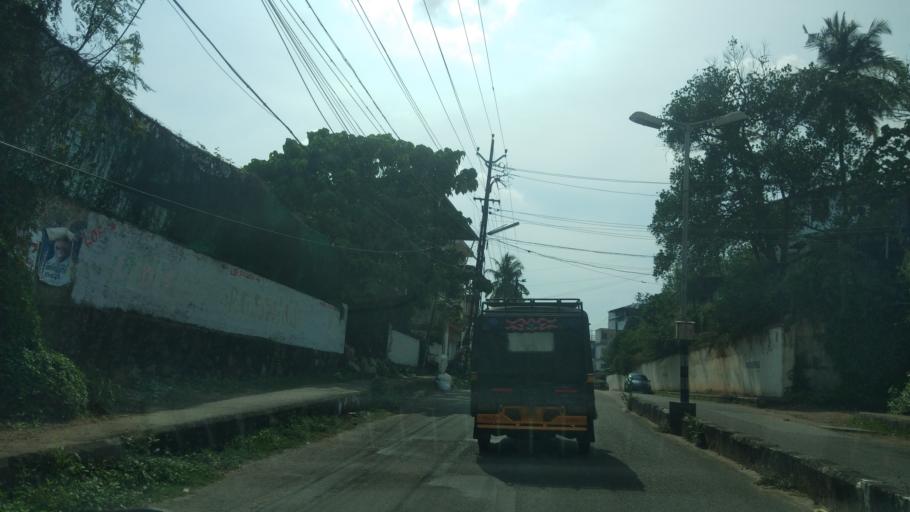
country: IN
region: Kerala
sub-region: Ernakulam
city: Elur
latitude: 10.0470
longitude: 76.3201
